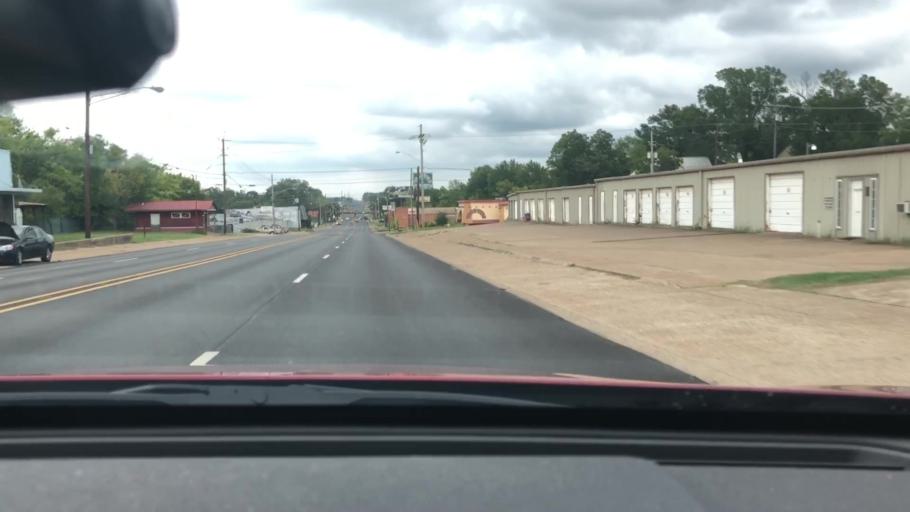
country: US
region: Arkansas
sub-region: Miller County
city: Texarkana
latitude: 33.4309
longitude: -94.0339
